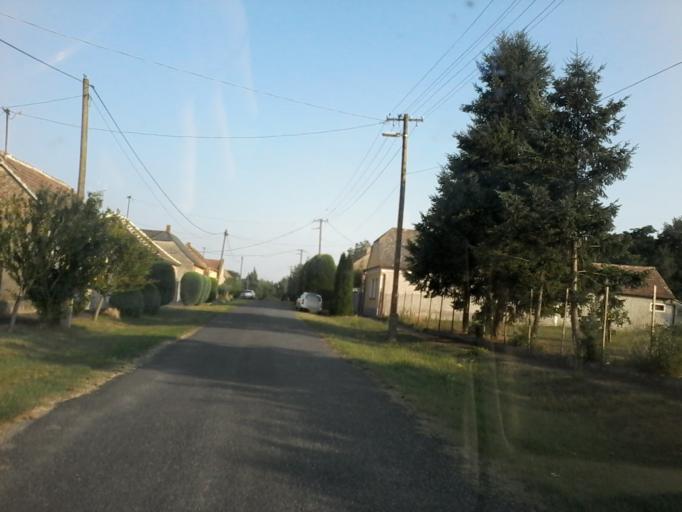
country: HU
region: Vas
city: Janoshaza
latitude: 47.1170
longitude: 17.2036
